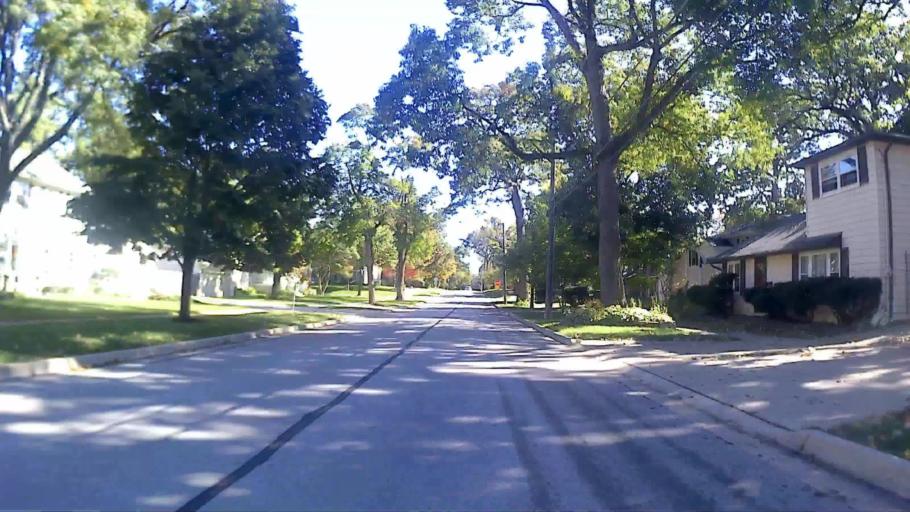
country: US
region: Illinois
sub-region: DuPage County
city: Glen Ellyn
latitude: 41.8773
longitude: -88.0540
